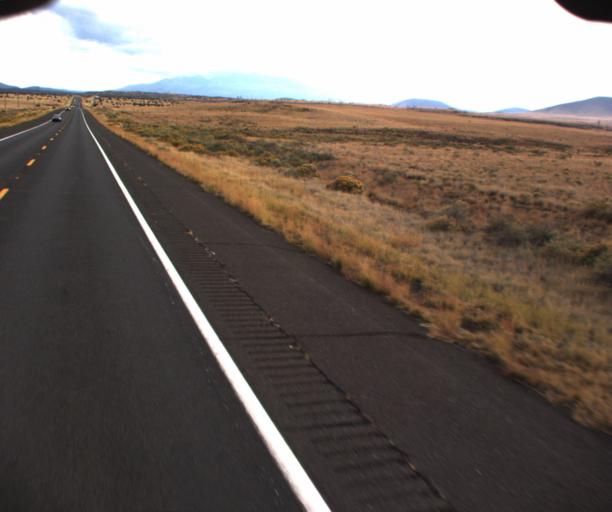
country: US
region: Arizona
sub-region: Coconino County
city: Flagstaff
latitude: 35.5593
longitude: -111.5346
